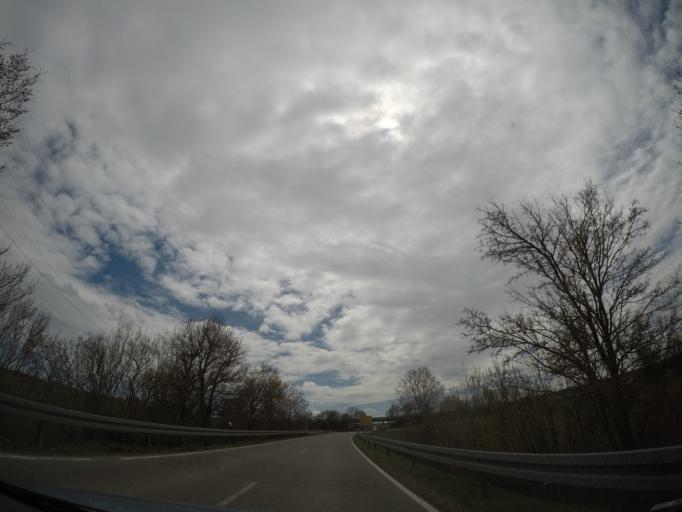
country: DE
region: Baden-Wuerttemberg
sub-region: Tuebingen Region
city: Laichingen
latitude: 48.4603
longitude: 9.7027
